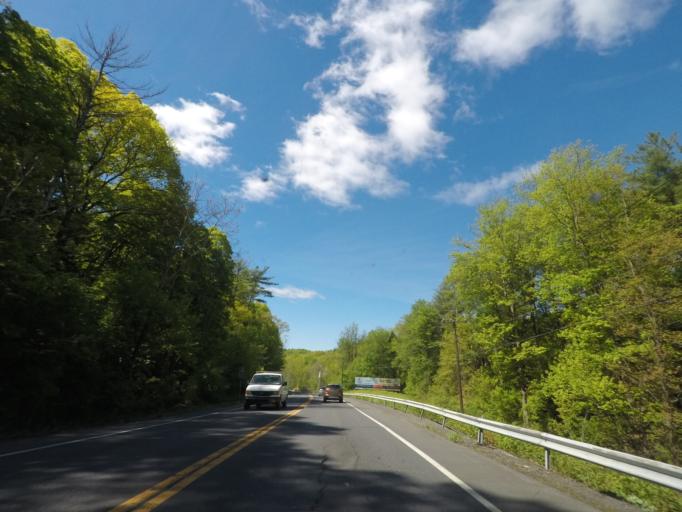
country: US
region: New York
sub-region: Ulster County
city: Glasco
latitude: 42.0396
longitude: -73.9692
